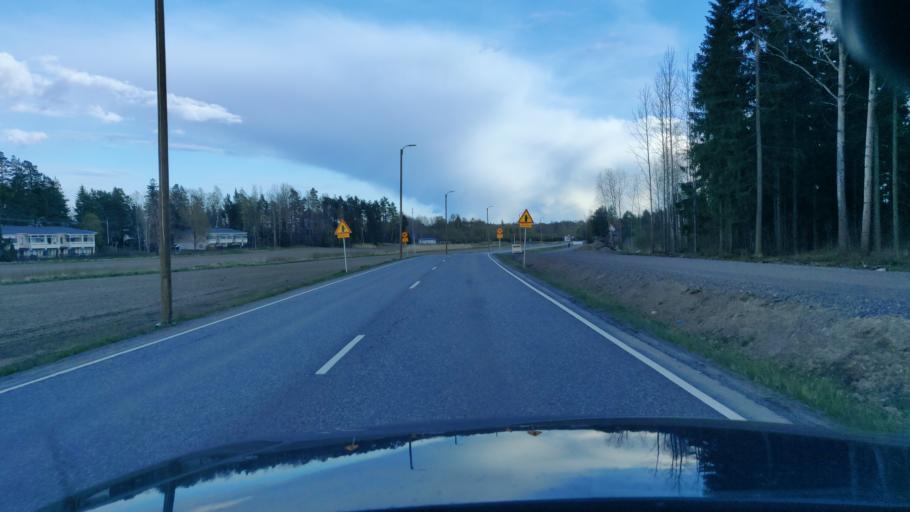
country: FI
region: Uusimaa
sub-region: Helsinki
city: Jaervenpaeae
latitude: 60.4728
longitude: 25.0682
